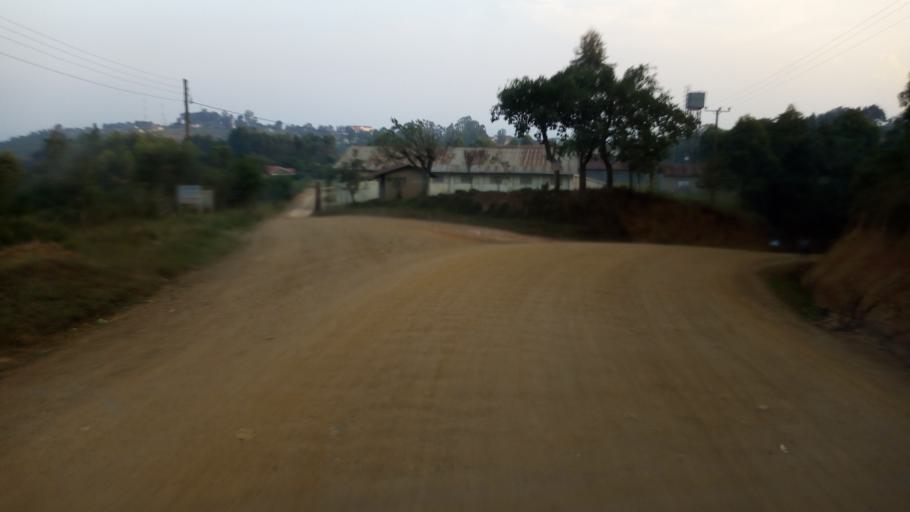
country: UG
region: Western Region
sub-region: Rukungiri District
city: Rukungiri
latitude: -0.7739
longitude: 29.9266
